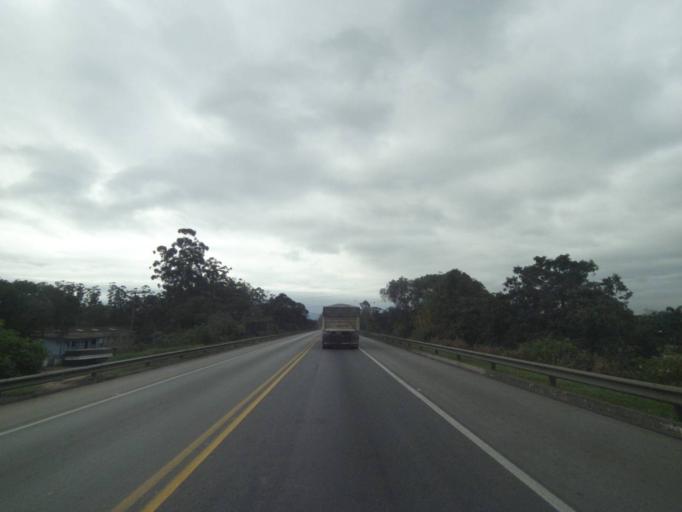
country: BR
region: Parana
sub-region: Paranagua
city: Paranagua
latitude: -25.5486
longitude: -48.5608
